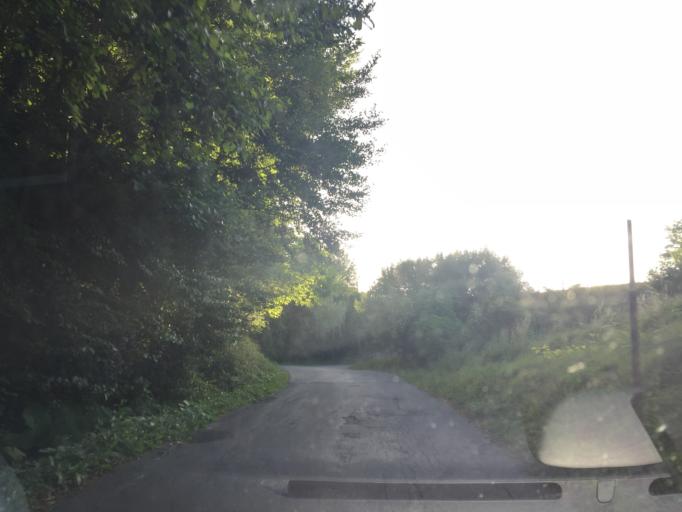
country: IT
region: Tuscany
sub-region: Provincia di Lucca
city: Castelnuovo di Garfagnana
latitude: 44.1192
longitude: 10.3910
